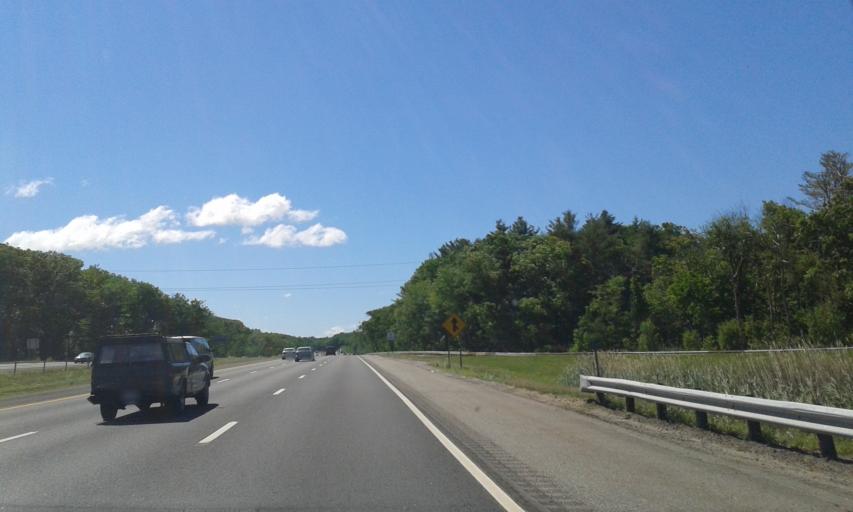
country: US
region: Massachusetts
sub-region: Middlesex County
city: Billerica
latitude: 42.5411
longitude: -71.2827
